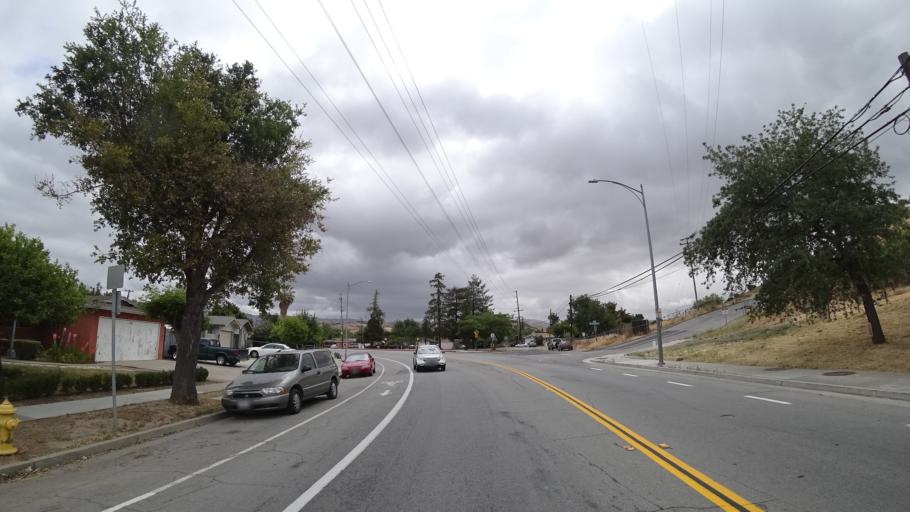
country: US
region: California
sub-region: Santa Clara County
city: Seven Trees
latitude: 37.2781
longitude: -121.8246
